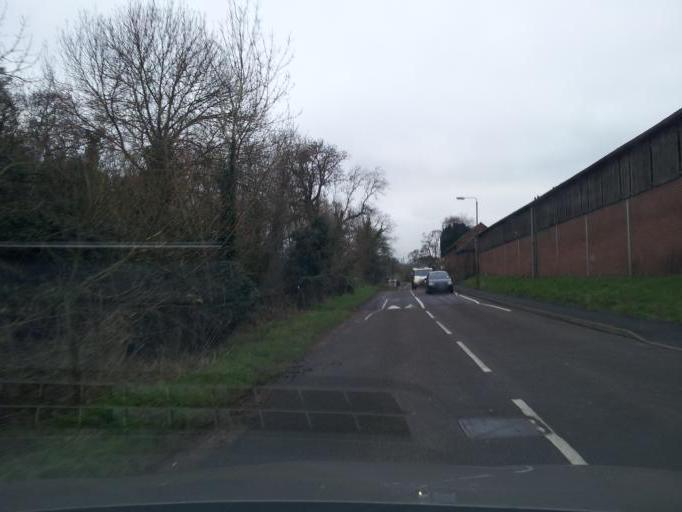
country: GB
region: England
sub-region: Derbyshire
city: Repton
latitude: 52.8310
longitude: -1.5416
